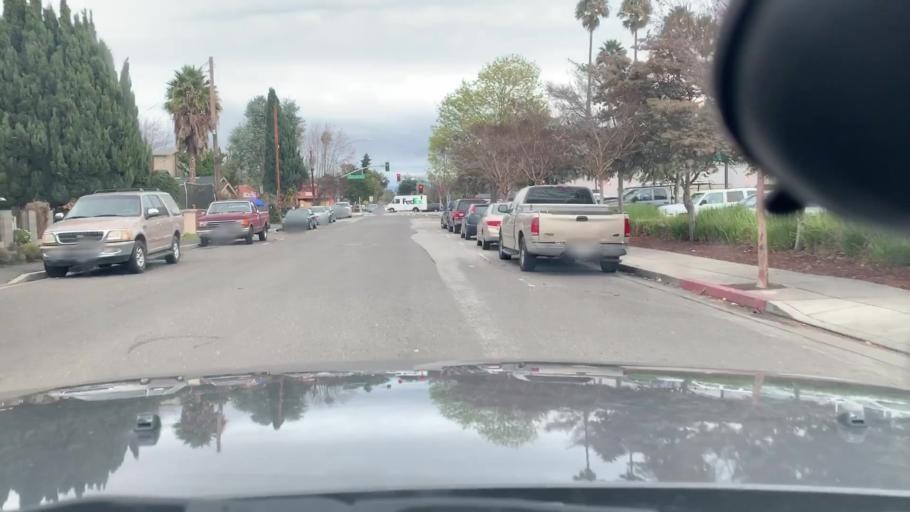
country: US
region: California
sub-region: San Mateo County
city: East Palo Alto
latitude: 37.4657
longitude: -122.1430
